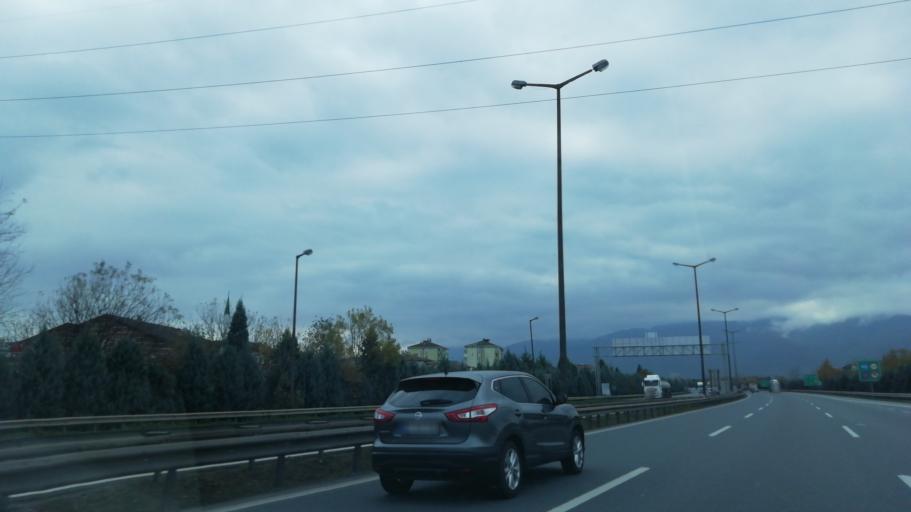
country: TR
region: Kocaeli
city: Kosekoy
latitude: 40.7437
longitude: 30.0429
